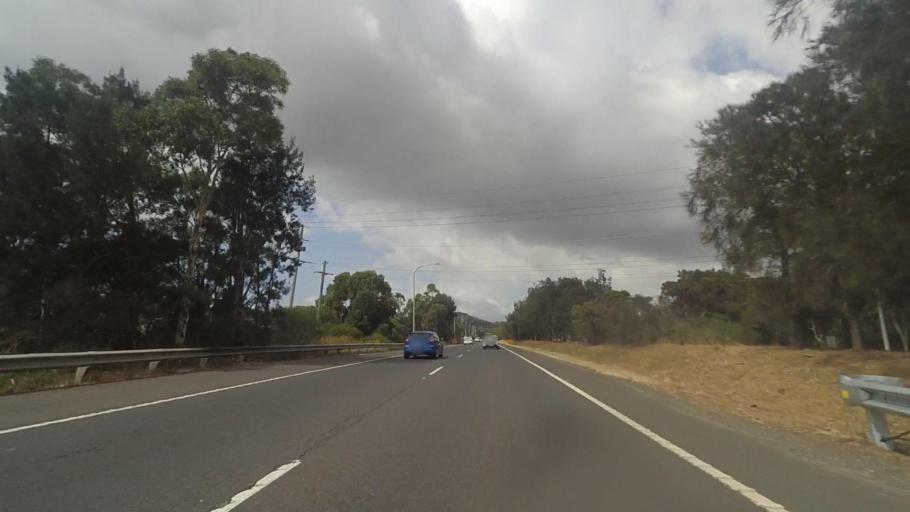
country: AU
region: New South Wales
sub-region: Wollongong
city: Mount Saint Thomas
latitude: -34.4551
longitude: 150.8574
